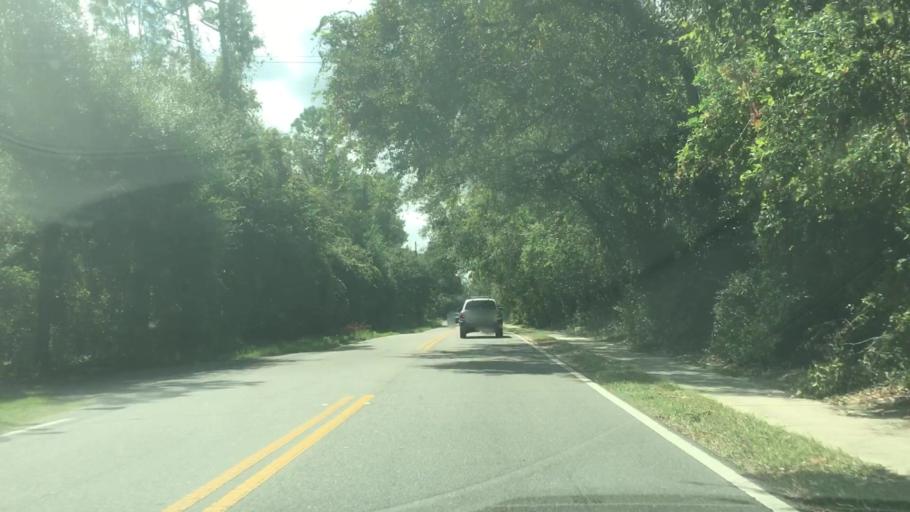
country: US
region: Florida
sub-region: Duval County
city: Jacksonville
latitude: 30.4479
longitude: -81.5792
